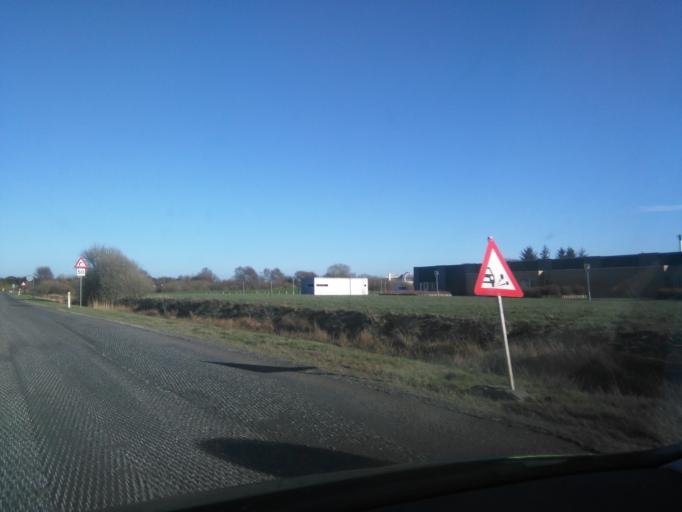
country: DK
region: Central Jutland
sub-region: Ringkobing-Skjern Kommune
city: Videbaek
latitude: 56.0966
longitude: 8.6428
